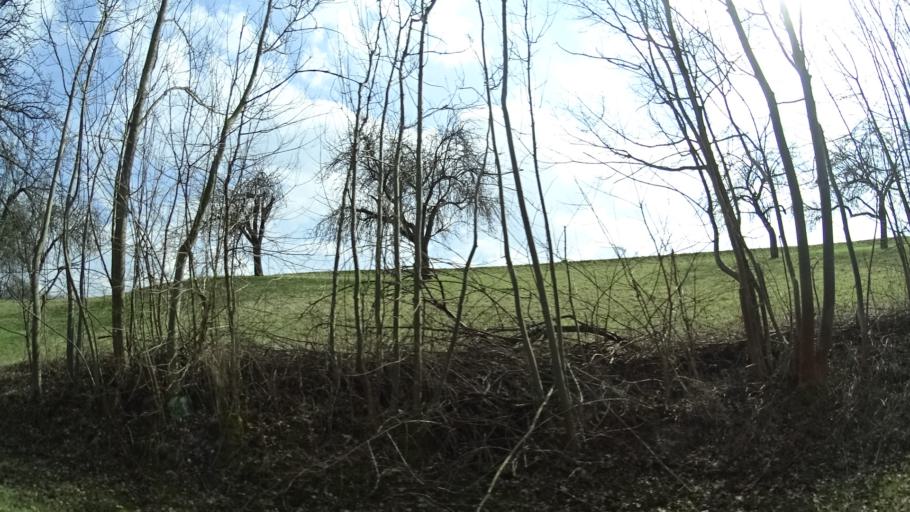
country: DE
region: Saxony-Anhalt
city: Schonburg
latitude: 51.1531
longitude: 11.8495
